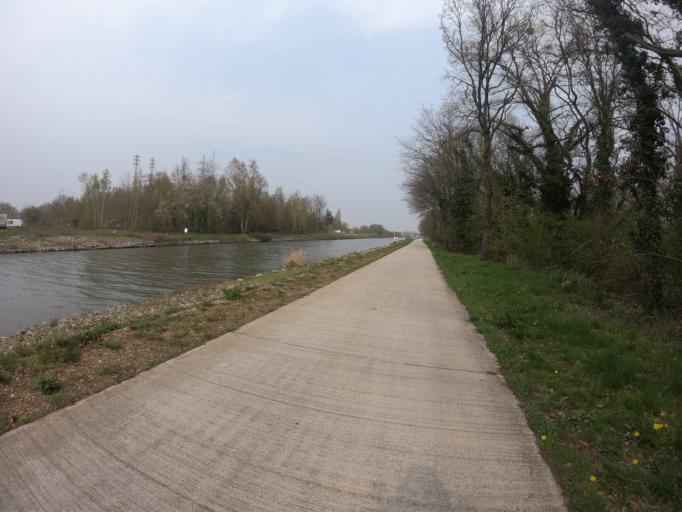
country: BE
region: Flanders
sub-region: Provincie Limburg
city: Maasmechelen
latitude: 51.0033
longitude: 5.7125
